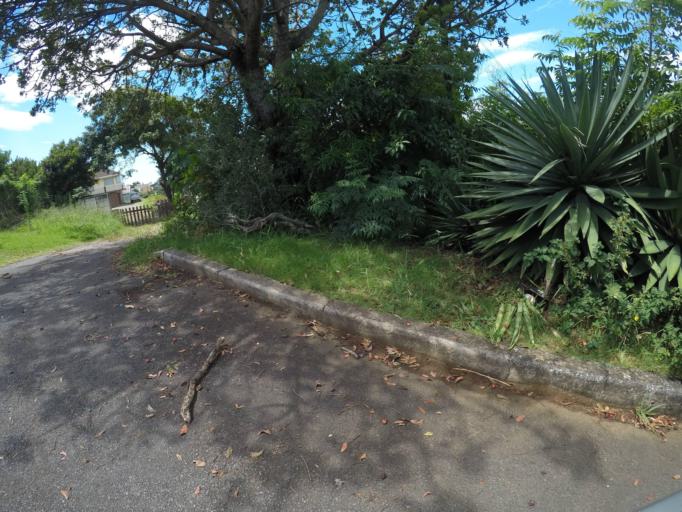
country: ZA
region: Eastern Cape
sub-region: Buffalo City Metropolitan Municipality
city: East London
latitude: -33.0368
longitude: 27.8574
